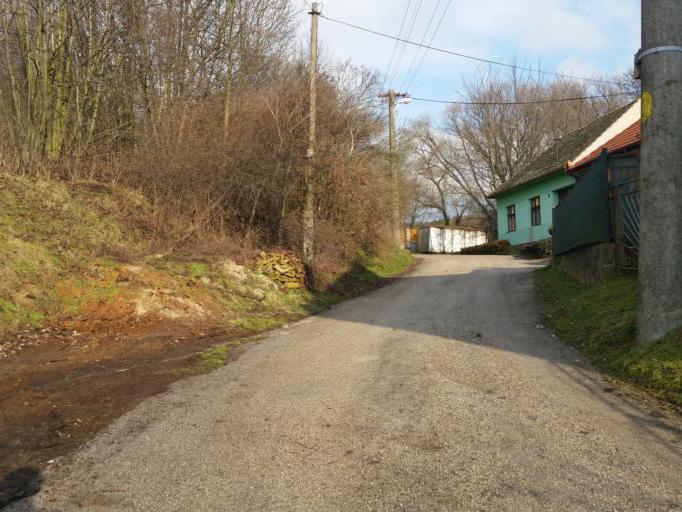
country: SK
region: Trnavsky
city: Vrbove
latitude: 48.6602
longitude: 17.7199
